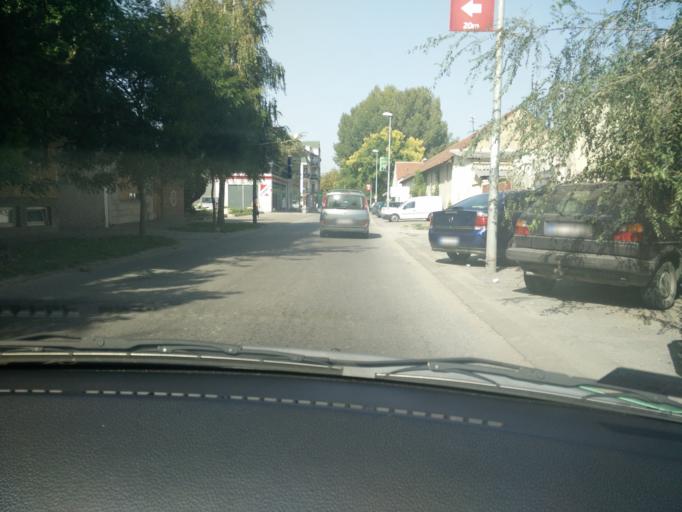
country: RS
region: Autonomna Pokrajina Vojvodina
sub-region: Juznobacki Okrug
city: Novi Sad
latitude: 45.2619
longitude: 19.8518
